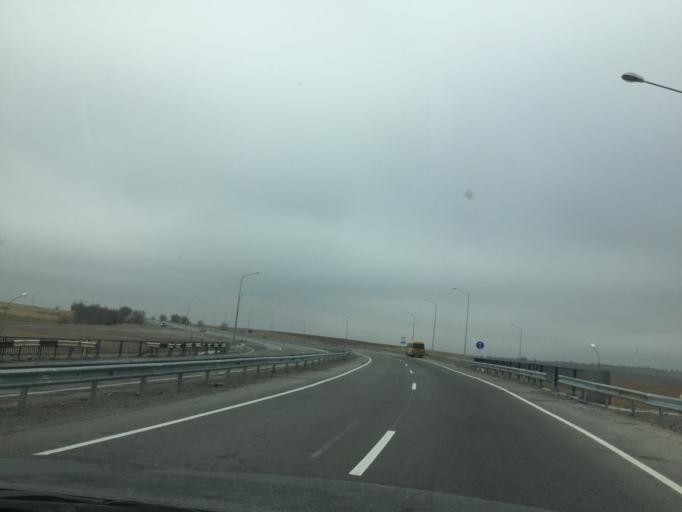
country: KZ
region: Ongtustik Qazaqstan
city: Aksu
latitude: 42.4729
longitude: 69.8983
